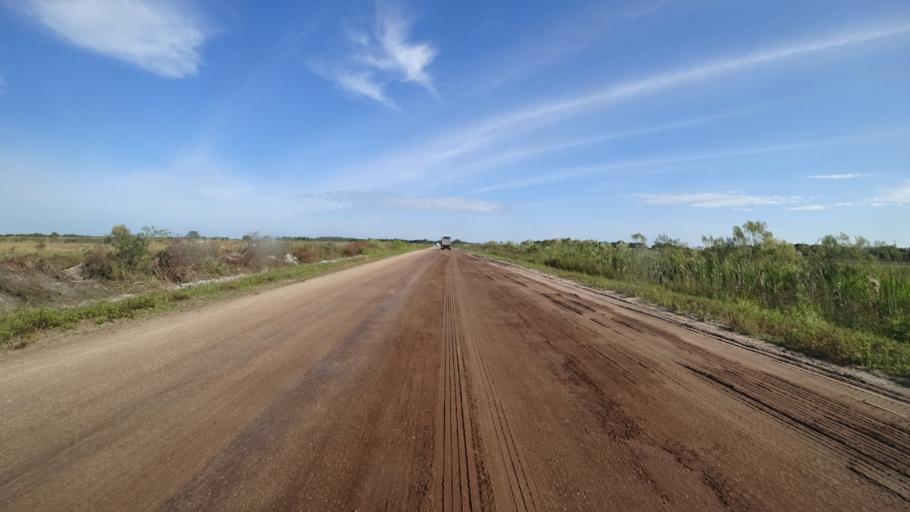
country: US
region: Florida
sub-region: Sarasota County
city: The Meadows
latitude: 27.4631
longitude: -82.3382
